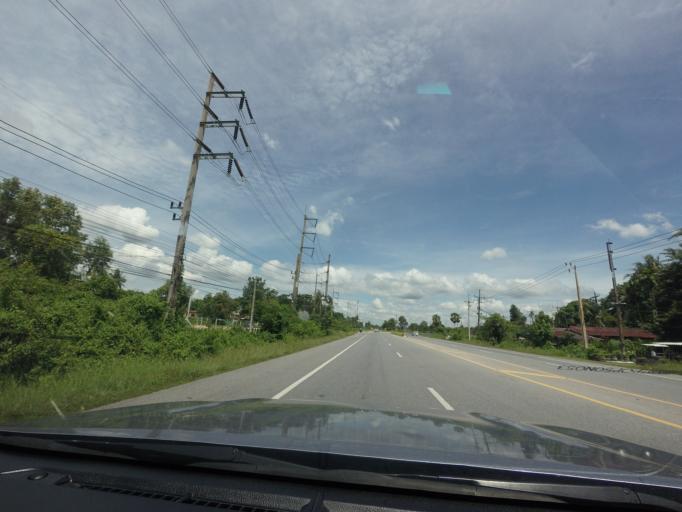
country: TH
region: Songkhla
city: Chana
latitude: 6.9841
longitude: 100.6800
